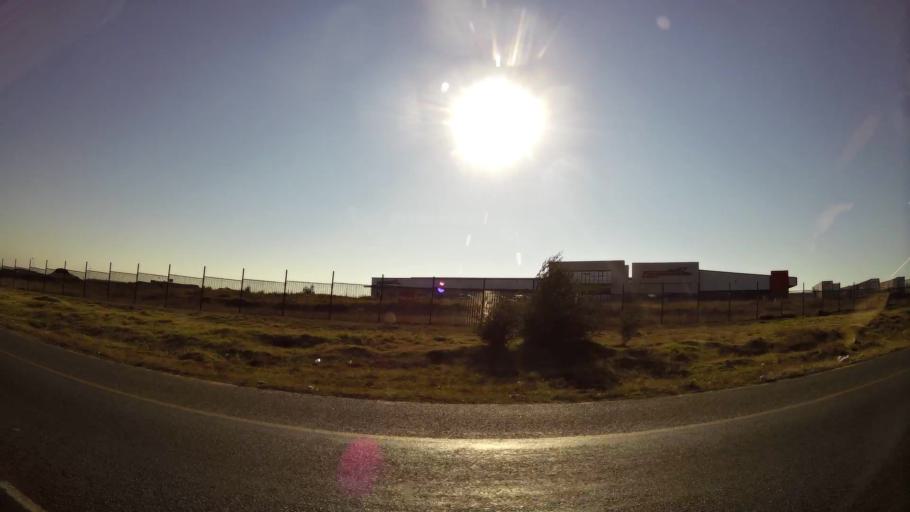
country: ZA
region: Gauteng
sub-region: City of Johannesburg Metropolitan Municipality
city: Modderfontein
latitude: -26.0558
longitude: 28.1647
